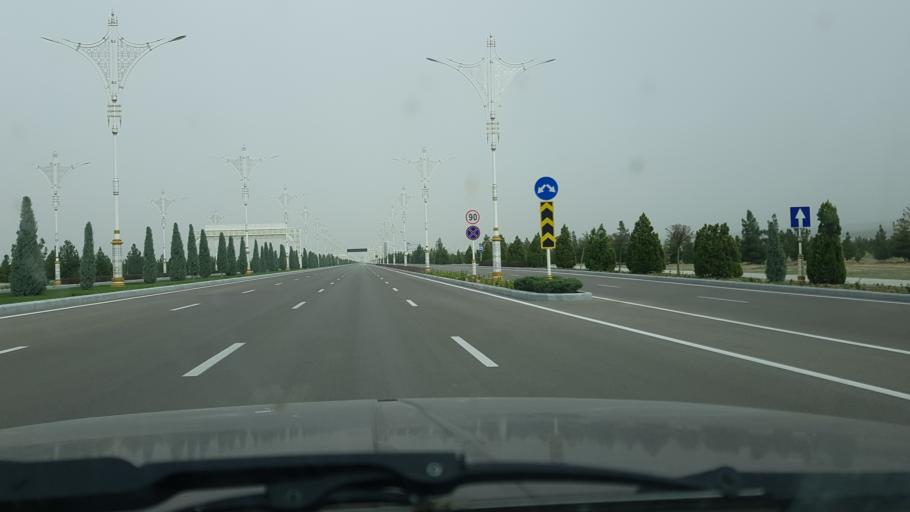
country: TM
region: Ahal
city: Ashgabat
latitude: 37.8959
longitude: 58.2593
